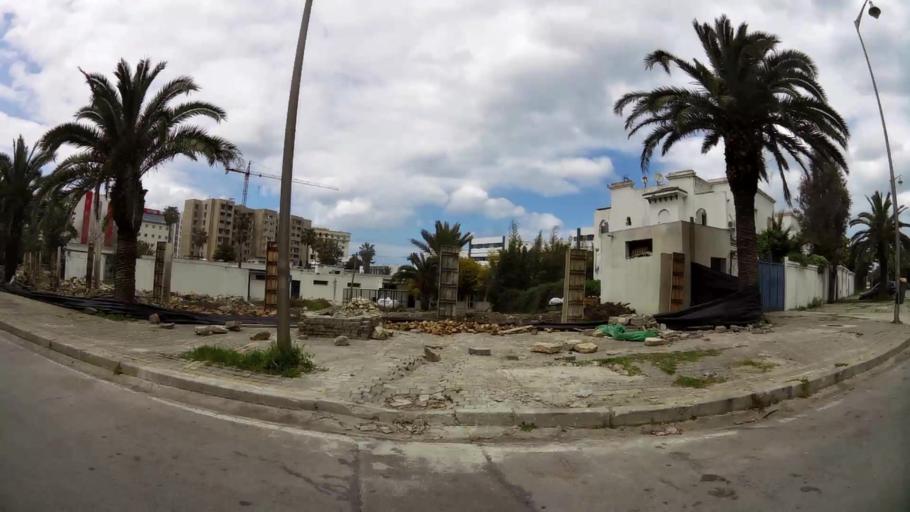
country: MA
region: Tanger-Tetouan
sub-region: Tanger-Assilah
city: Tangier
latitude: 35.7733
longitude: -5.7775
